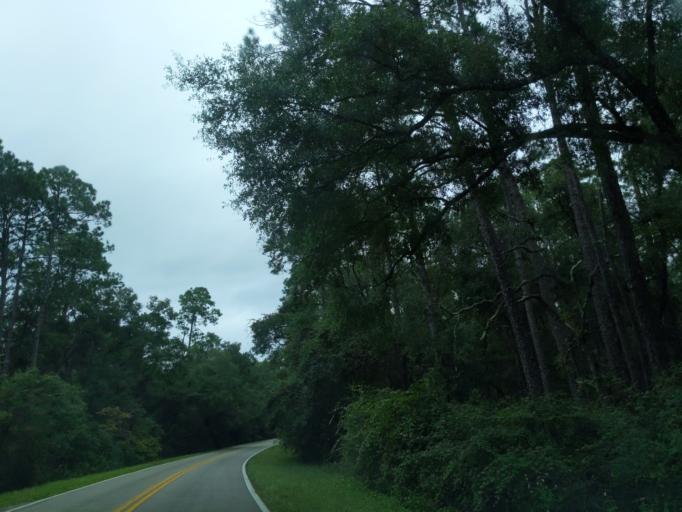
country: US
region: Florida
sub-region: Gadsden County
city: Midway
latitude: 30.4113
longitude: -84.4169
